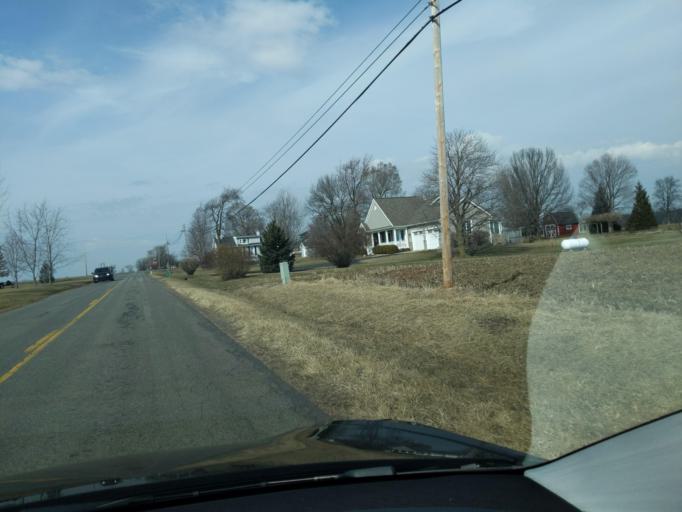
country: US
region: Michigan
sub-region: Ingham County
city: Williamston
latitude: 42.6588
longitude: -84.3096
